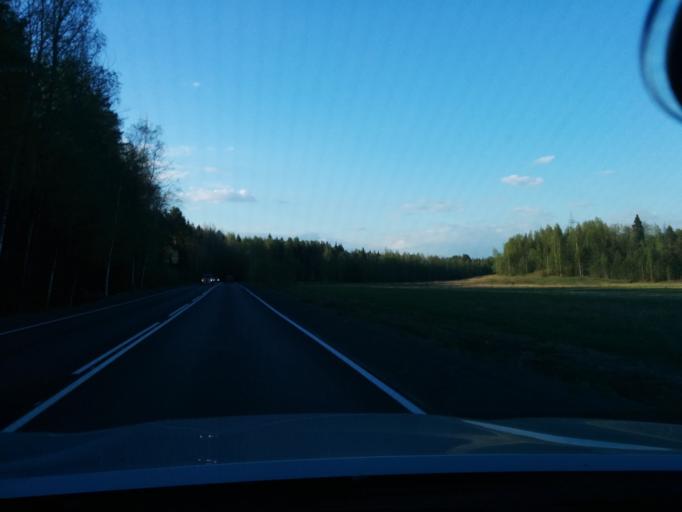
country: RU
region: Leningrad
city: Verkhniye Osel'ki
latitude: 60.1926
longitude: 30.4146
